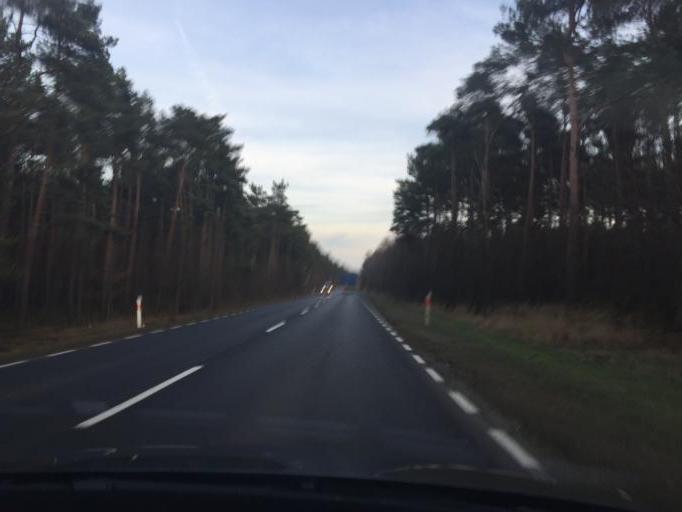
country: PL
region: Lubusz
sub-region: Powiat zielonogorski
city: Nowogrod Bobrzanski
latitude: 51.8125
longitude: 15.2714
